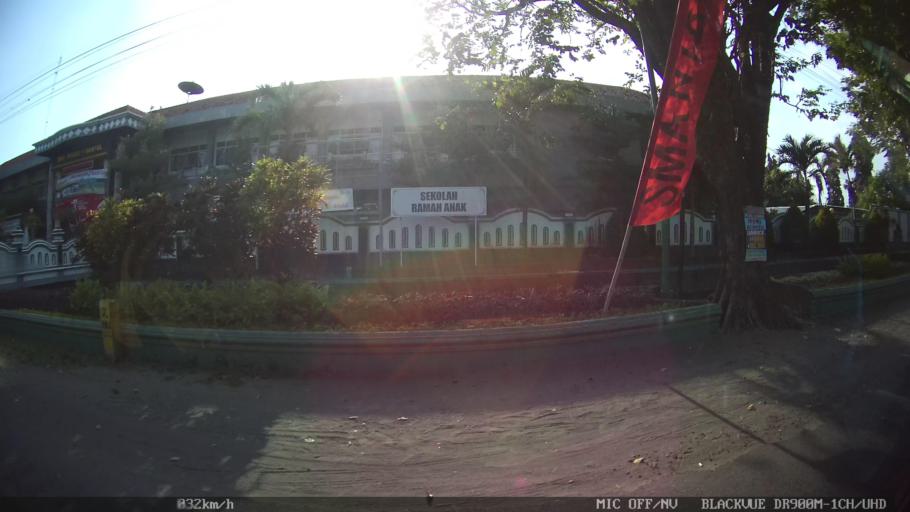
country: ID
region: Daerah Istimewa Yogyakarta
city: Bantul
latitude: -7.8982
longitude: 110.3227
